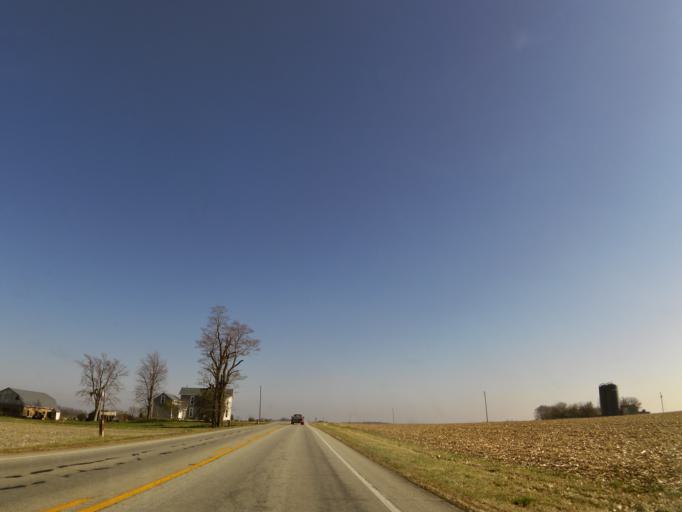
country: US
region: Indiana
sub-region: Fayette County
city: Connersville
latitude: 39.6277
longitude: -85.2681
